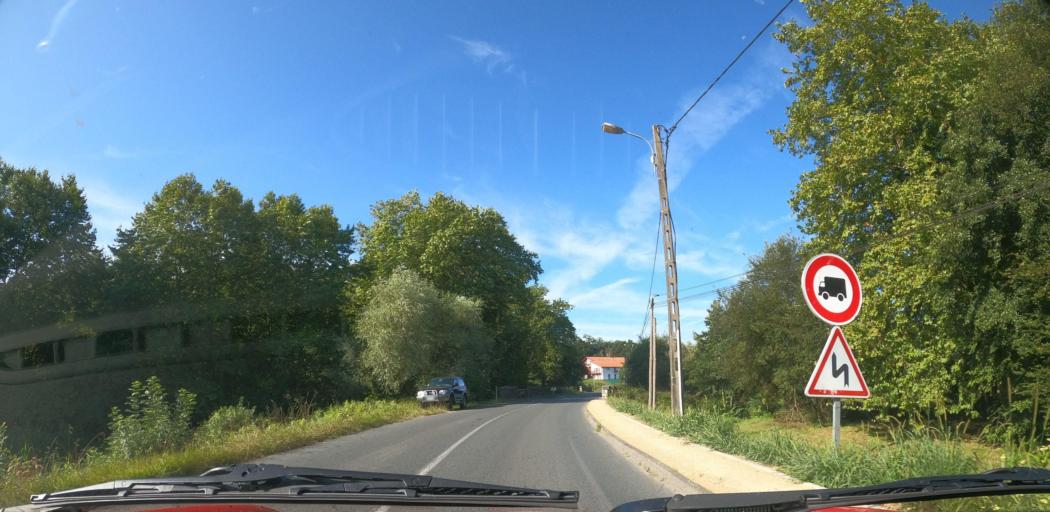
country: FR
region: Aquitaine
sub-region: Departement des Pyrenees-Atlantiques
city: Arbonne
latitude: 43.4368
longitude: -1.5513
